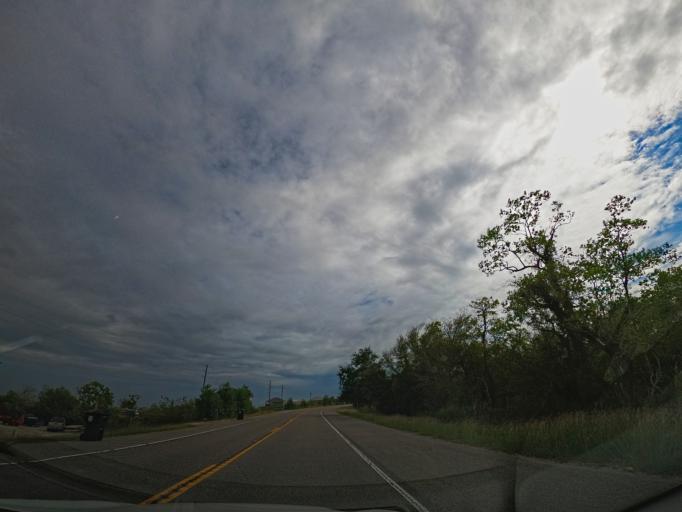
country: US
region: Louisiana
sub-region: Saint Tammany Parish
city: Eden Isle
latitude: 30.1169
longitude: -89.7623
